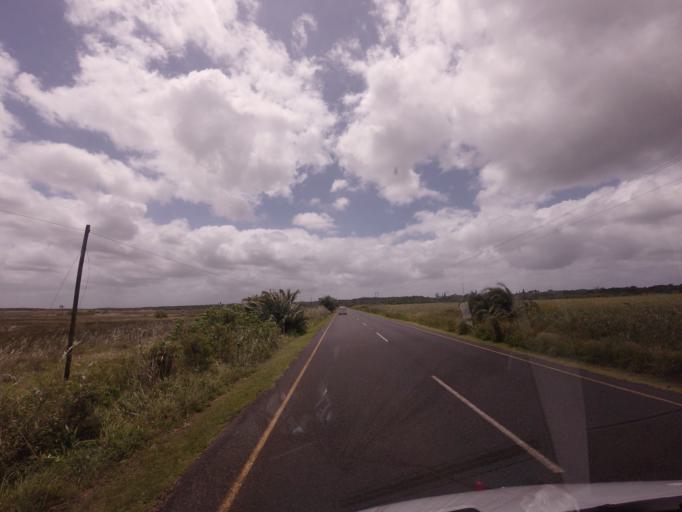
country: ZA
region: KwaZulu-Natal
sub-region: uMkhanyakude District Municipality
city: Mtubatuba
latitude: -28.3721
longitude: 32.4011
